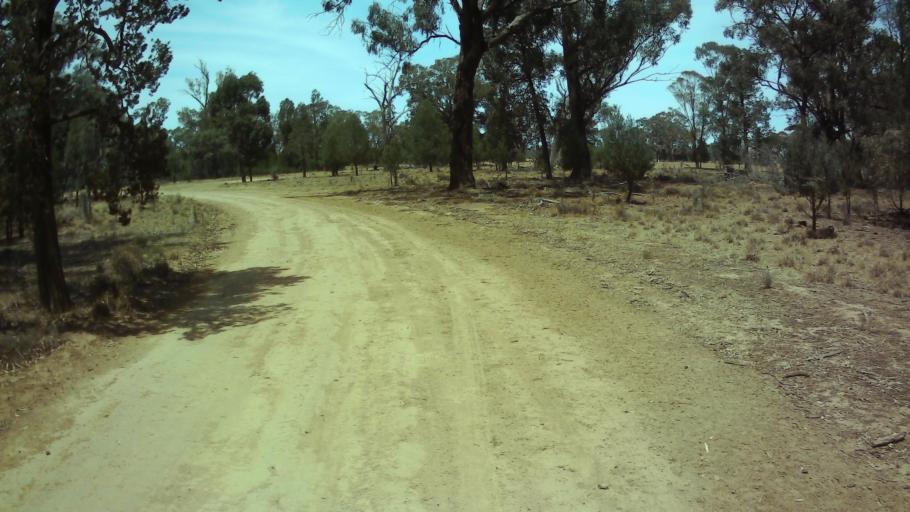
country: AU
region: New South Wales
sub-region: Weddin
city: Grenfell
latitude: -34.0359
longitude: 147.9243
